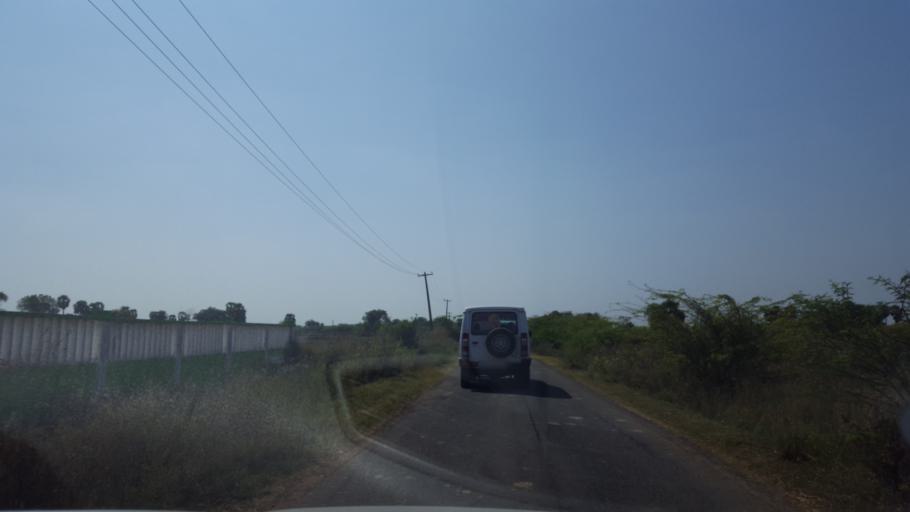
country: IN
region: Tamil Nadu
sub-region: Kancheepuram
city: Wallajahbad
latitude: 12.8584
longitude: 79.7833
